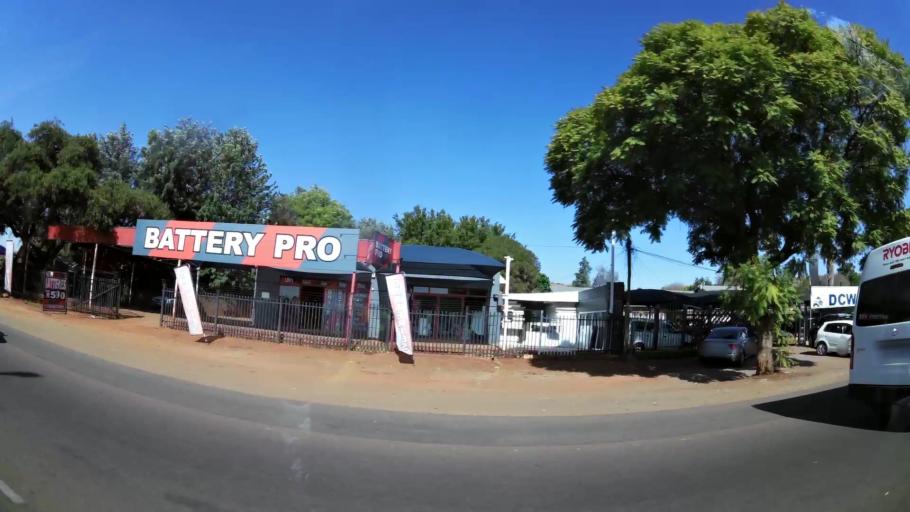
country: ZA
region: Gauteng
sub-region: City of Tshwane Metropolitan Municipality
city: Pretoria
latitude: -25.6802
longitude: 28.2352
